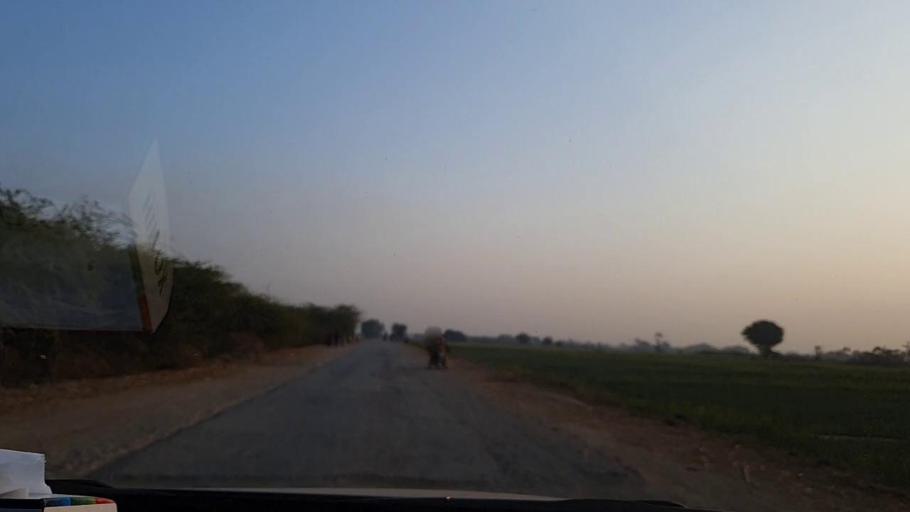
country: PK
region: Sindh
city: Tando Ghulam Ali
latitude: 25.1789
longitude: 68.9490
